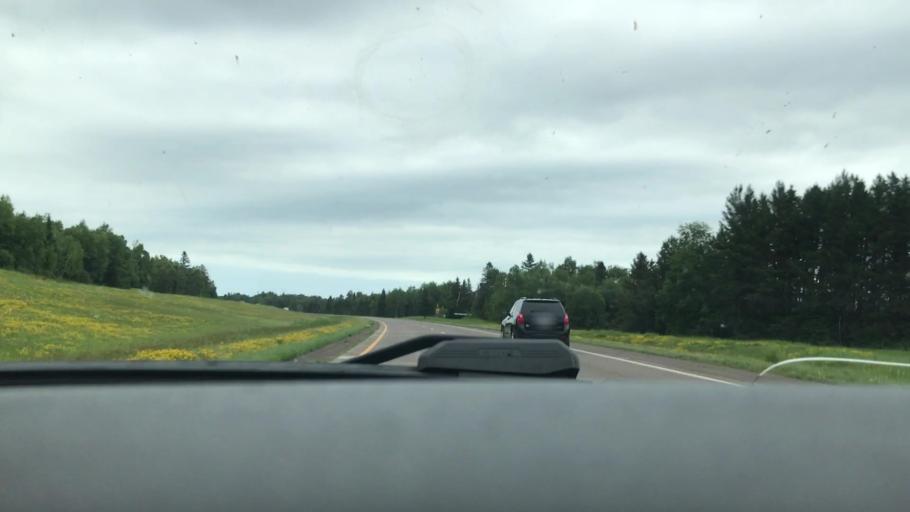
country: US
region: Minnesota
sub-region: Lake County
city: Two Harbors
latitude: 46.9303
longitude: -91.8326
